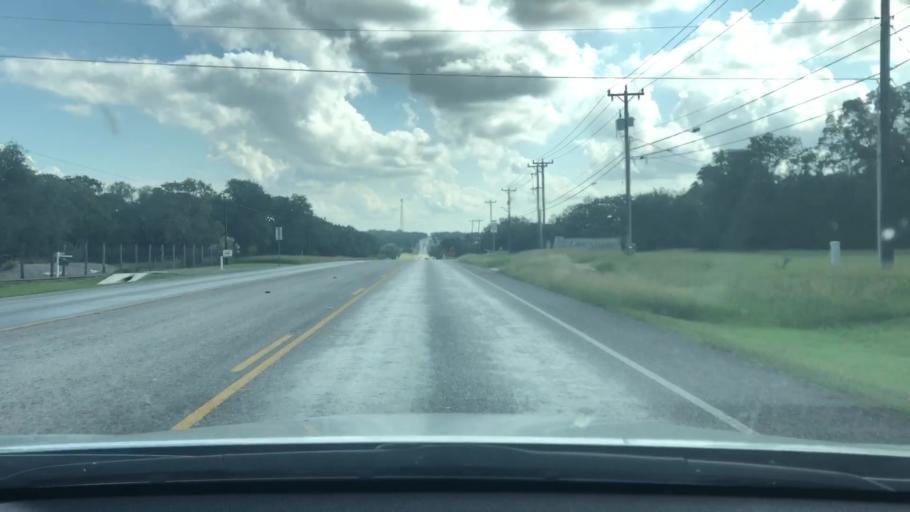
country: US
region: Texas
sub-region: Bexar County
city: Fair Oaks Ranch
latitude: 29.7492
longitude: -98.6234
